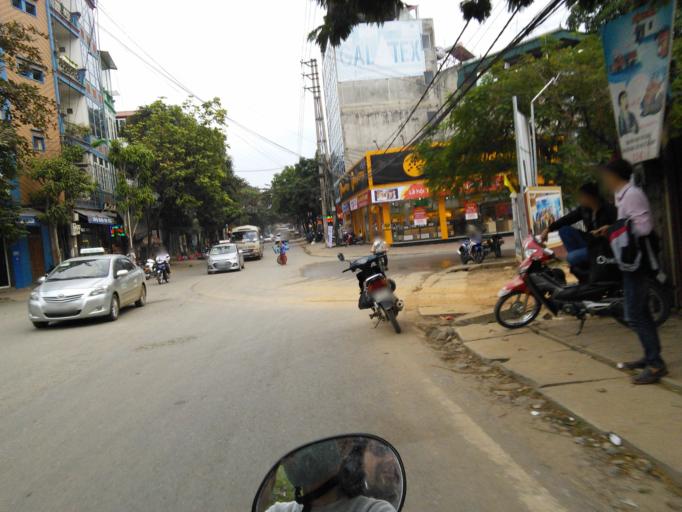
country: VN
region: Lao Cai
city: Lao Cai
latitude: 22.4940
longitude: 103.9762
